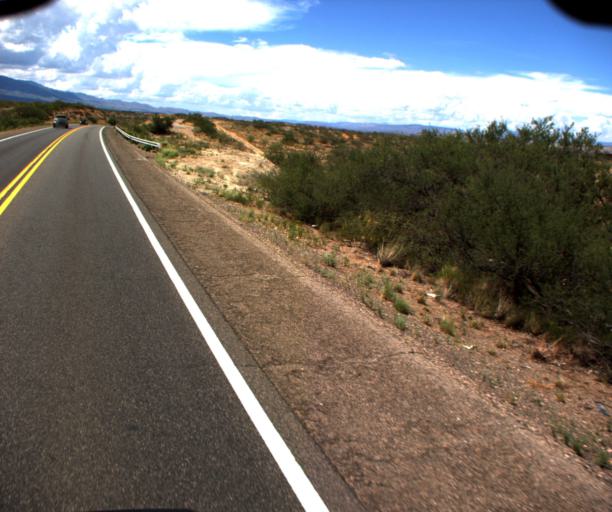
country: US
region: Arizona
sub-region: Yavapai County
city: Camp Verde
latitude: 34.6021
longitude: -111.9050
